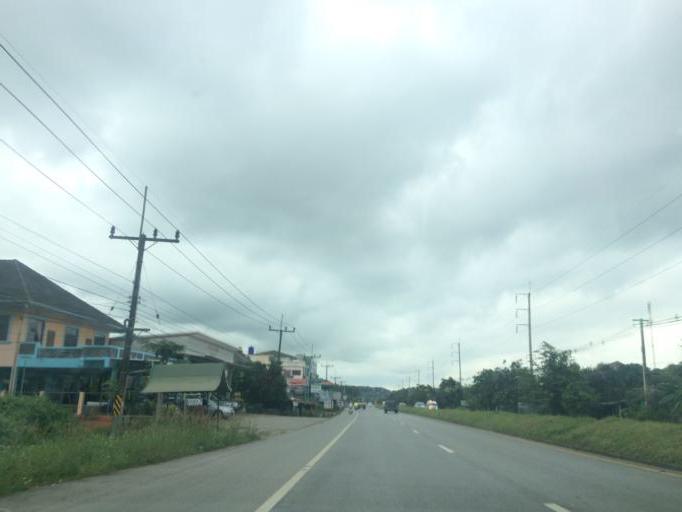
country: TH
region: Chiang Rai
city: Mae Chan
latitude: 20.0959
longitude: 99.8745
